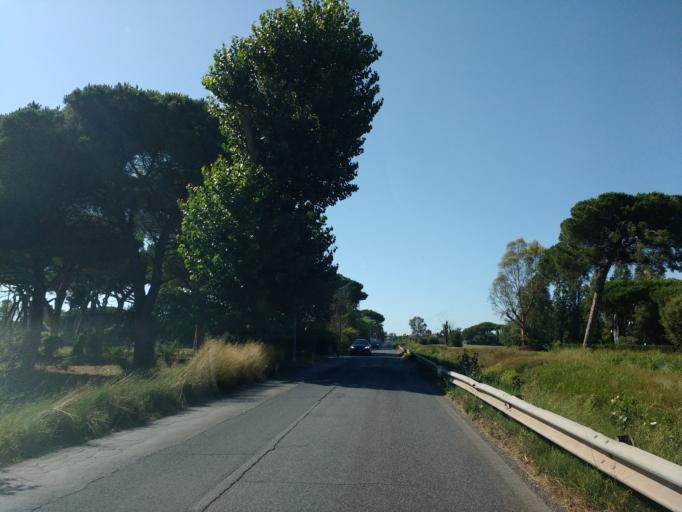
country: IT
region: Latium
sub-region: Citta metropolitana di Roma Capitale
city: Acilia-Castel Fusano-Ostia Antica
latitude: 41.7421
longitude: 12.3394
